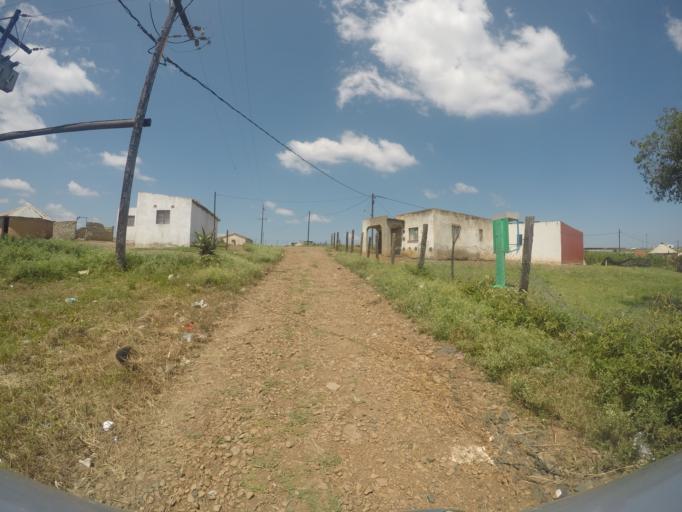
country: ZA
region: KwaZulu-Natal
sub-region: uThungulu District Municipality
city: Empangeni
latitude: -28.6098
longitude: 31.7353
